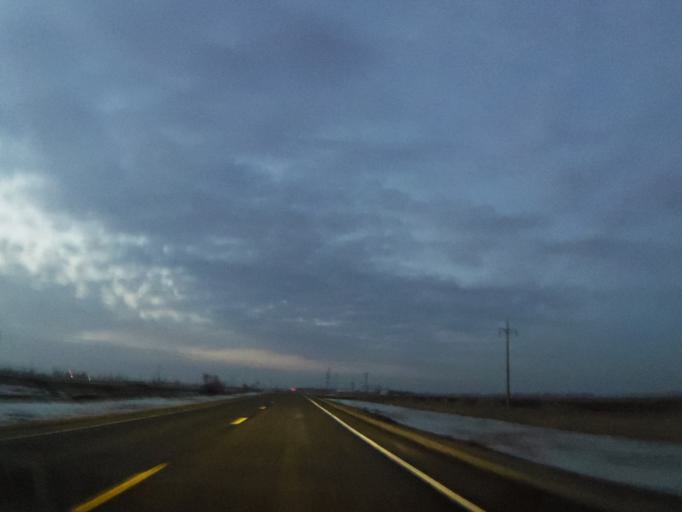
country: US
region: North Dakota
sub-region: Walsh County
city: Park River
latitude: 48.2055
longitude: -97.6226
